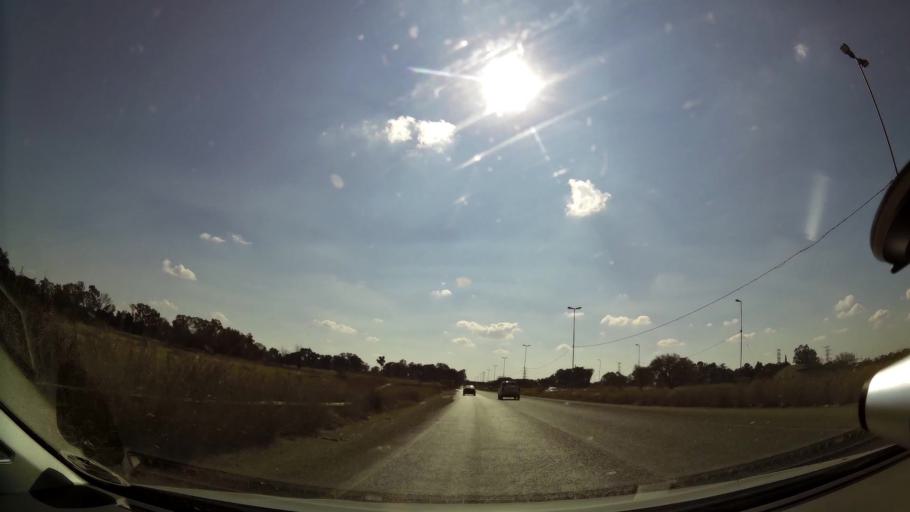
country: ZA
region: Orange Free State
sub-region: Mangaung Metropolitan Municipality
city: Bloemfontein
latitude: -29.1209
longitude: 26.2671
